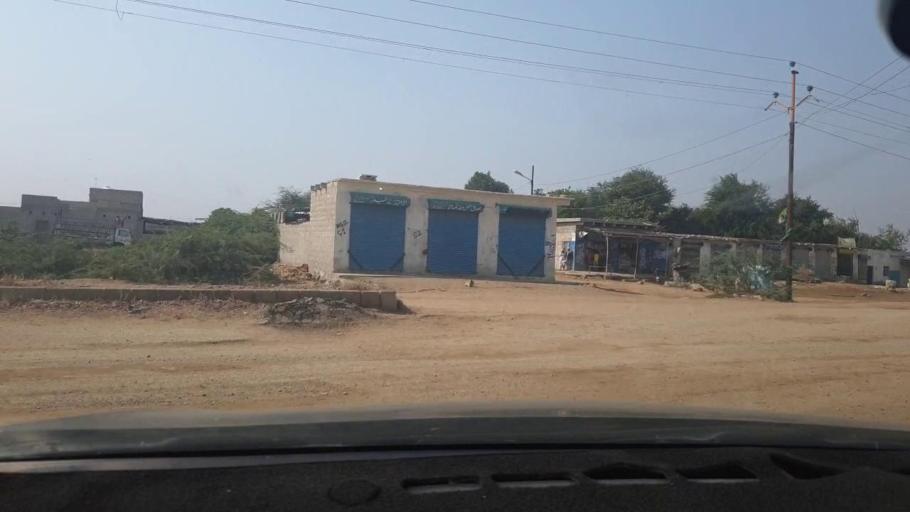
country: PK
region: Sindh
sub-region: Karachi District
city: Karachi
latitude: 25.0028
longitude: 66.9708
